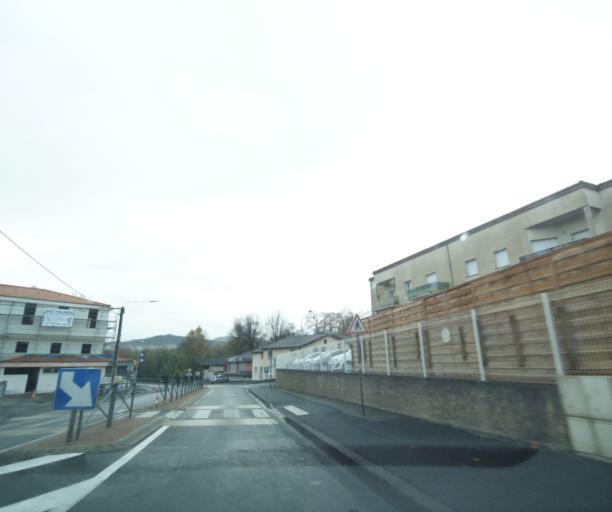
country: FR
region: Auvergne
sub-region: Departement du Puy-de-Dome
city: Cournon-d'Auvergne
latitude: 45.7308
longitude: 3.2115
